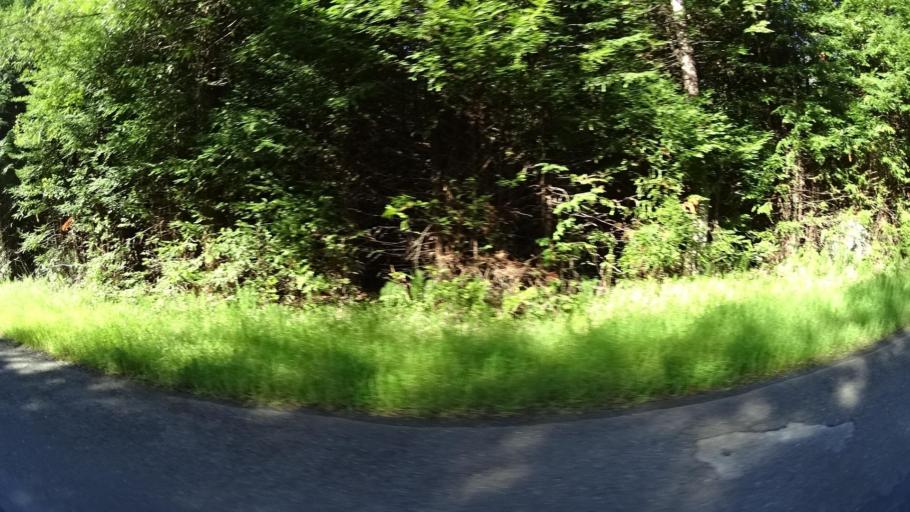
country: US
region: California
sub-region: Humboldt County
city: Rio Dell
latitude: 40.4554
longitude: -124.0318
